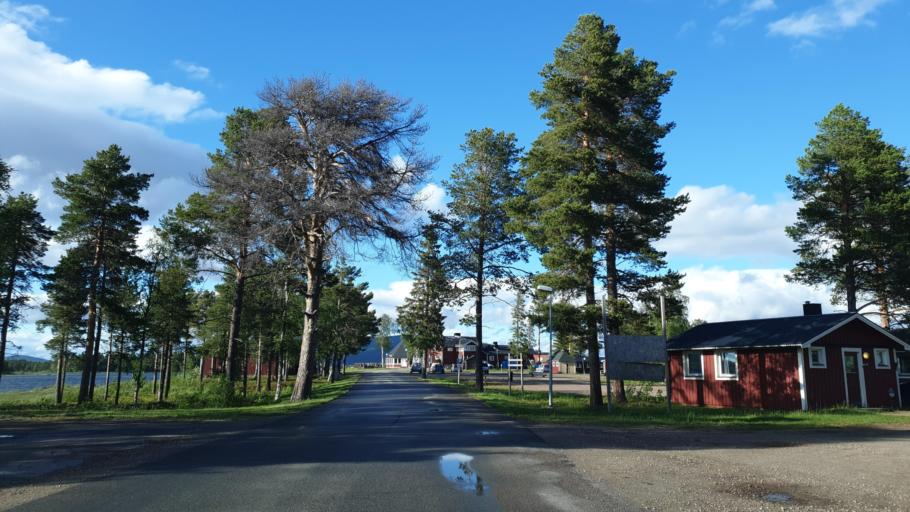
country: SE
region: Norrbotten
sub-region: Arjeplogs Kommun
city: Arjeplog
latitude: 66.0517
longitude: 17.8650
